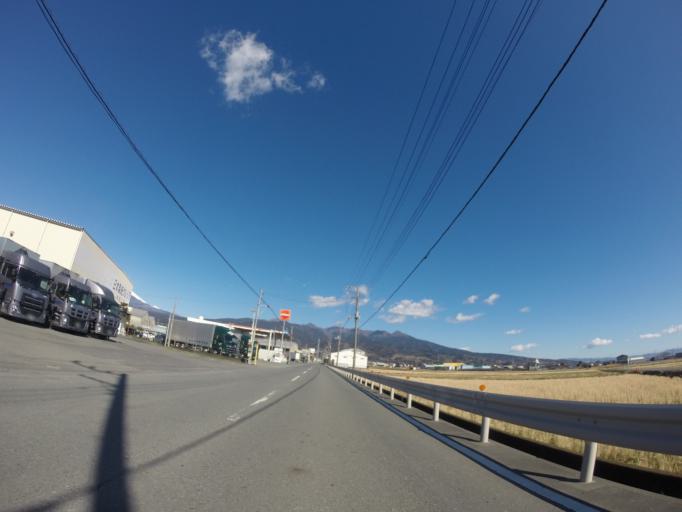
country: JP
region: Shizuoka
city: Fuji
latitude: 35.1544
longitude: 138.7187
